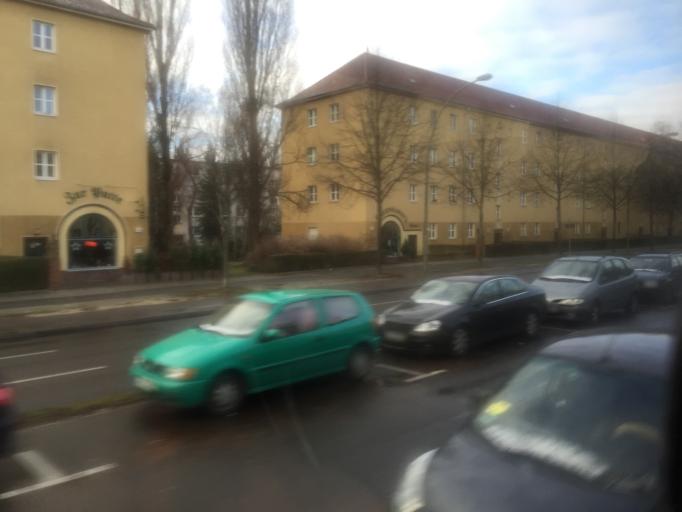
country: DE
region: Berlin
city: Plaenterwald
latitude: 52.4766
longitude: 13.4804
